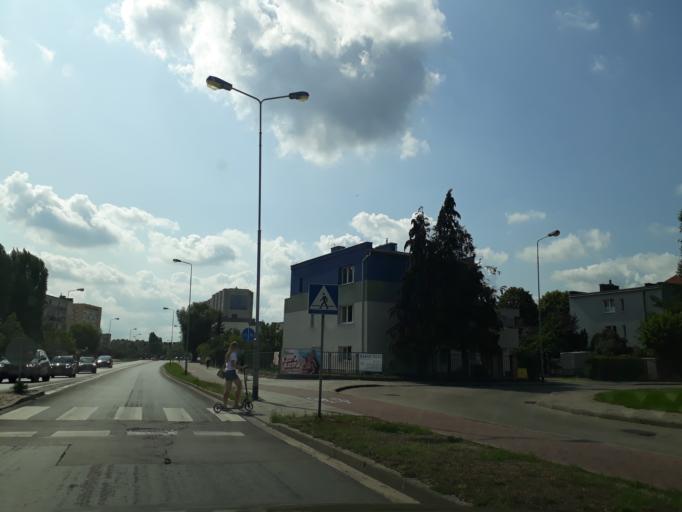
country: PL
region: West Pomeranian Voivodeship
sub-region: Swinoujscie
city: Swinoujscie
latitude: 53.9067
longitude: 14.2343
